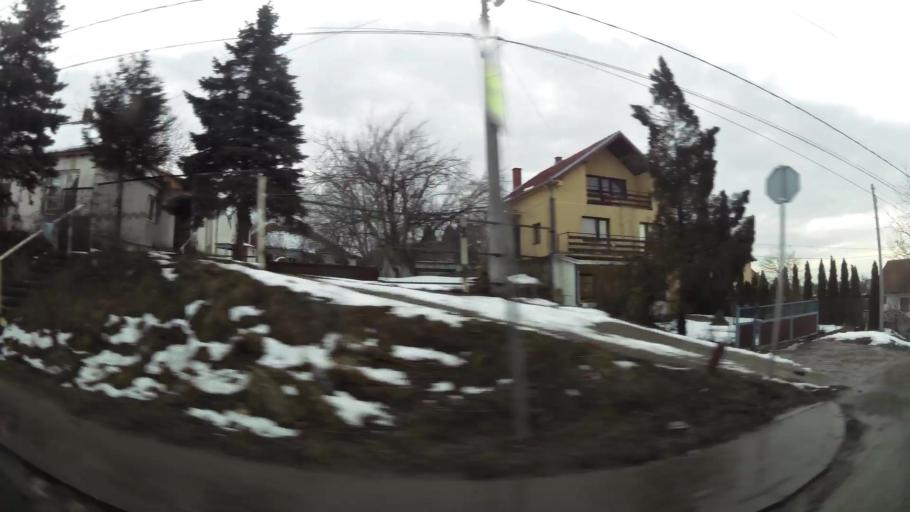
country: RS
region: Central Serbia
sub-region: Belgrade
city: Rakovica
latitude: 44.7227
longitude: 20.4958
